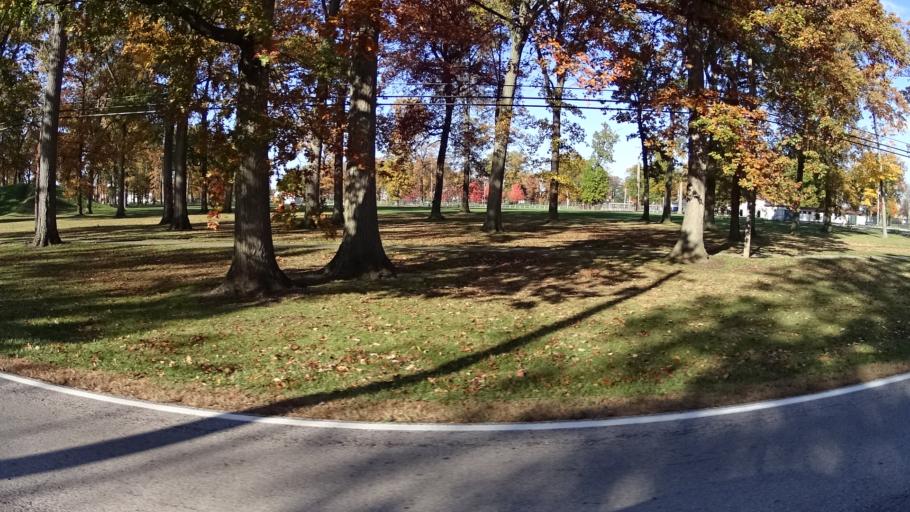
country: US
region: Ohio
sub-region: Lorain County
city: Sheffield
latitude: 41.4380
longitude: -82.1254
